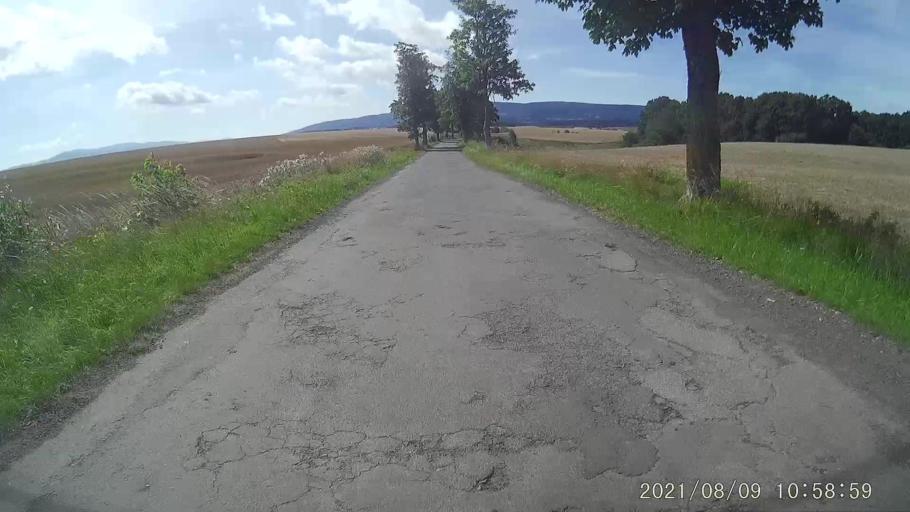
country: PL
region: Lower Silesian Voivodeship
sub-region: Powiat klodzki
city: Polanica-Zdroj
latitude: 50.4463
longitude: 16.5495
